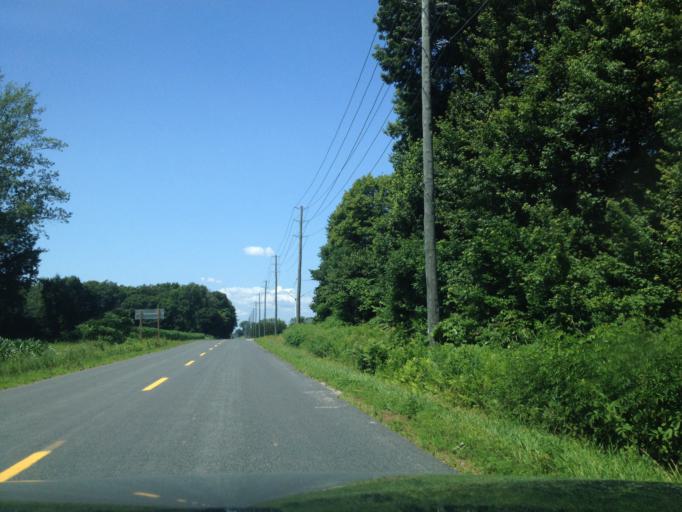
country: CA
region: Ontario
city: Aylmer
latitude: 42.6391
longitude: -80.7246
